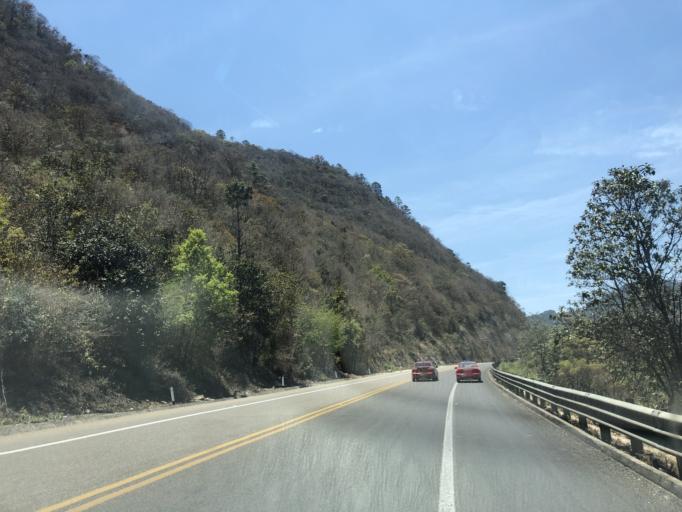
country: MX
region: Chiapas
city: San Cristobal de las Casas
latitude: 16.7197
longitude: -92.6680
